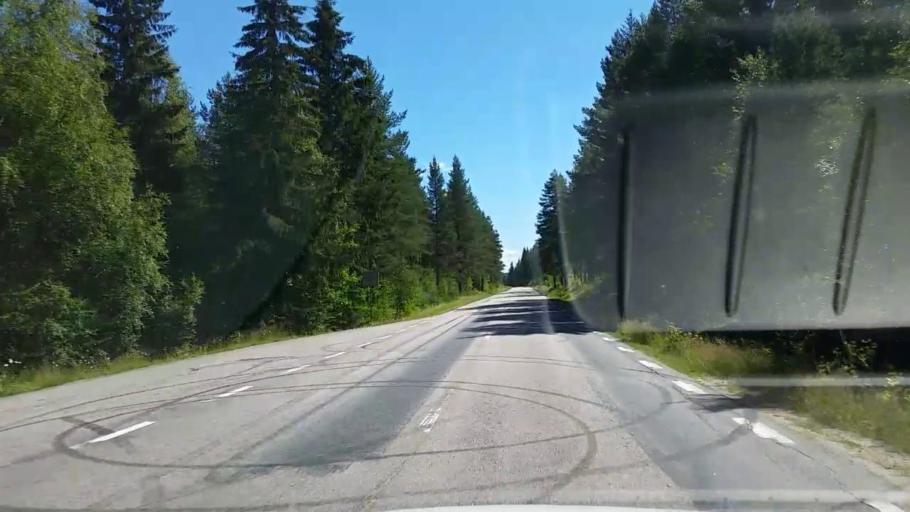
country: SE
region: Gaevleborg
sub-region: Ovanakers Kommun
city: Edsbyn
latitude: 61.3529
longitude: 15.8139
